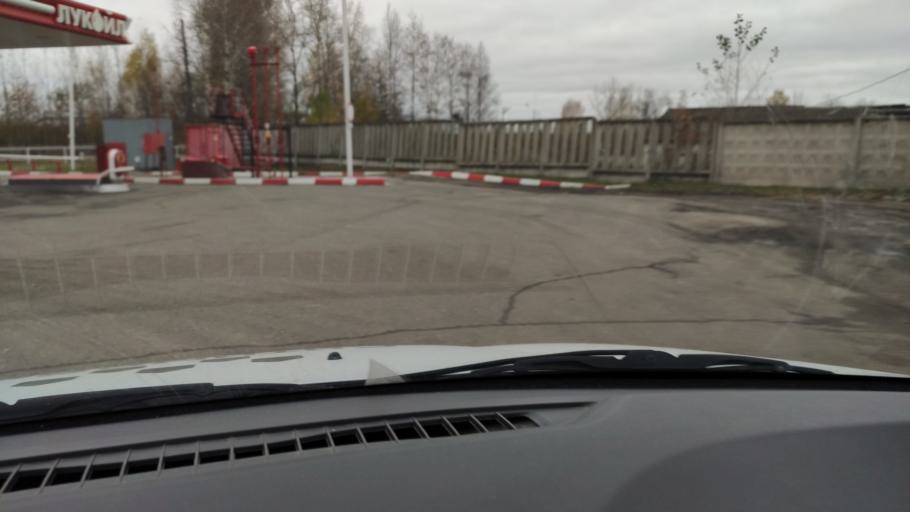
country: RU
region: Kirov
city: Slobodskoy
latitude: 58.7190
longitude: 50.1753
